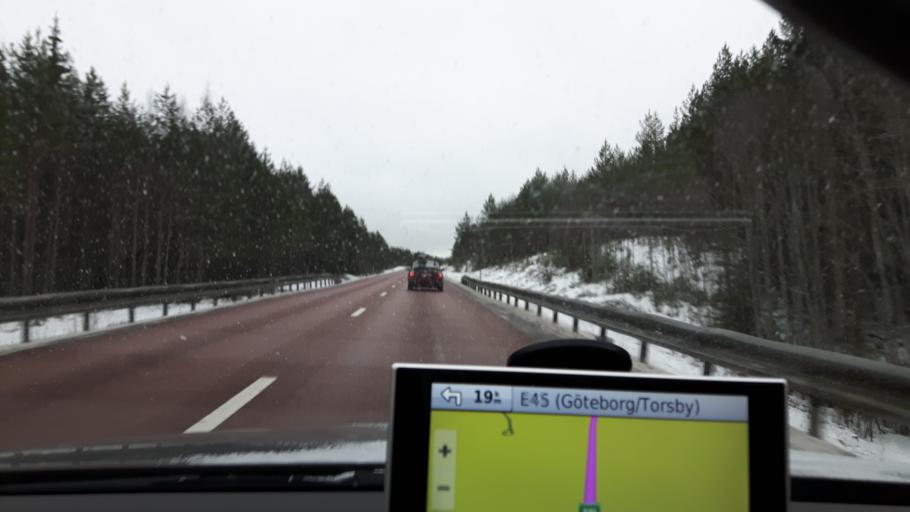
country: SE
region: Vaermland
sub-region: Hagfors Kommun
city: Ekshaerad
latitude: 60.4023
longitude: 13.2606
